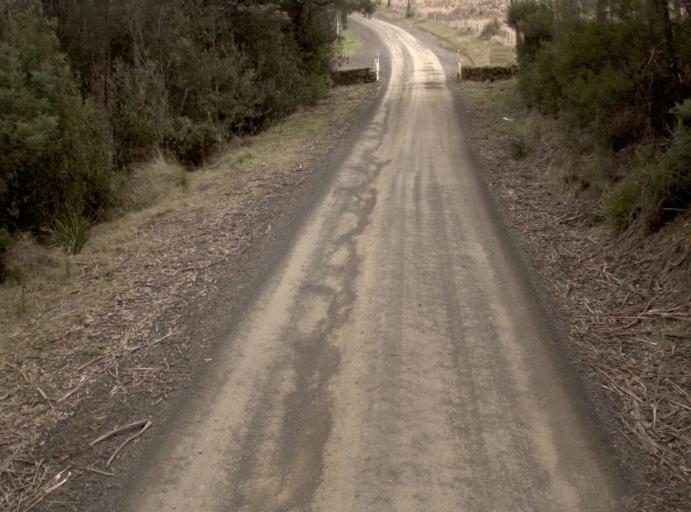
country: AU
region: Tasmania
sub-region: Launceston
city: Newstead
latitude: -41.3940
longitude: 147.3039
